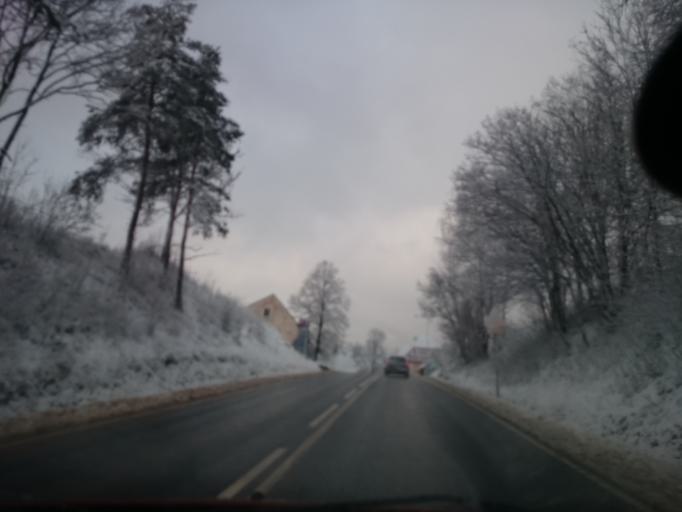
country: PL
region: Lower Silesian Voivodeship
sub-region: Powiat klodzki
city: Bystrzyca Klodzka
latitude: 50.3531
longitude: 16.6662
